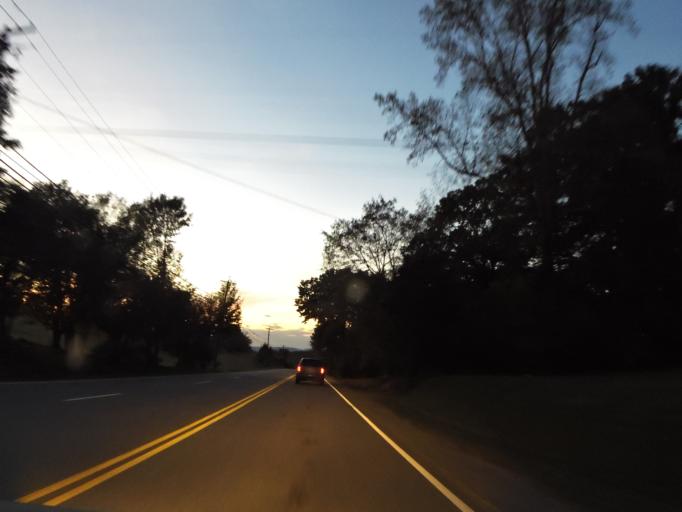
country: US
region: Tennessee
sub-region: Knox County
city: Mascot
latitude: 36.0216
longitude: -83.7009
